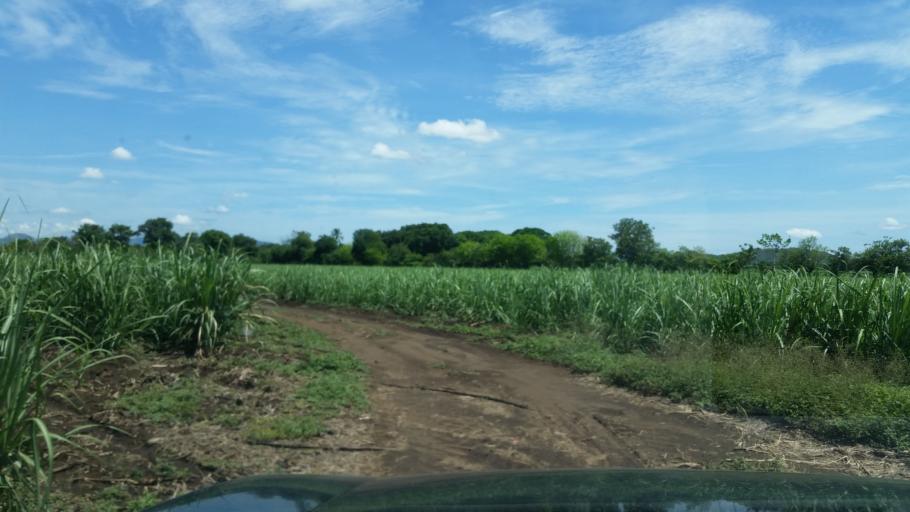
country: NI
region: Chinandega
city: Puerto Morazan
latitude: 12.7722
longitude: -87.1220
